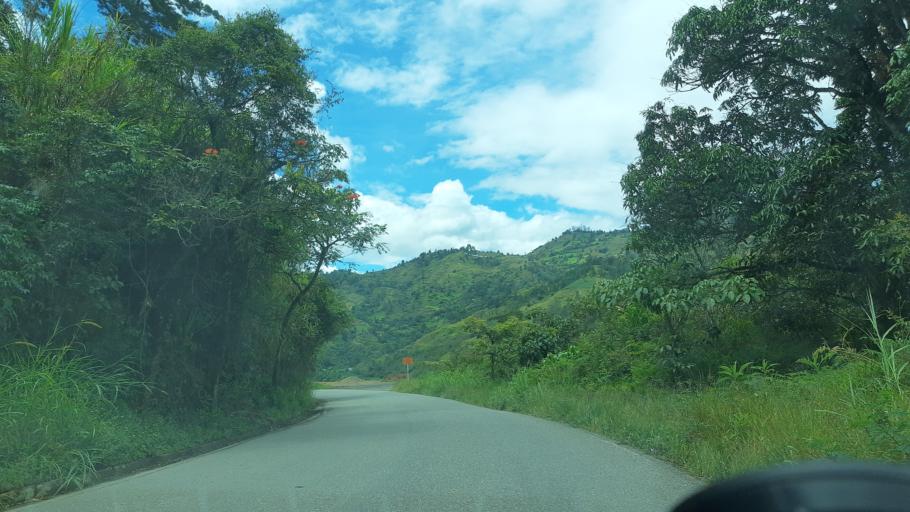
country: CO
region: Boyaca
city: Garagoa
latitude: 5.0445
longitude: -73.3879
